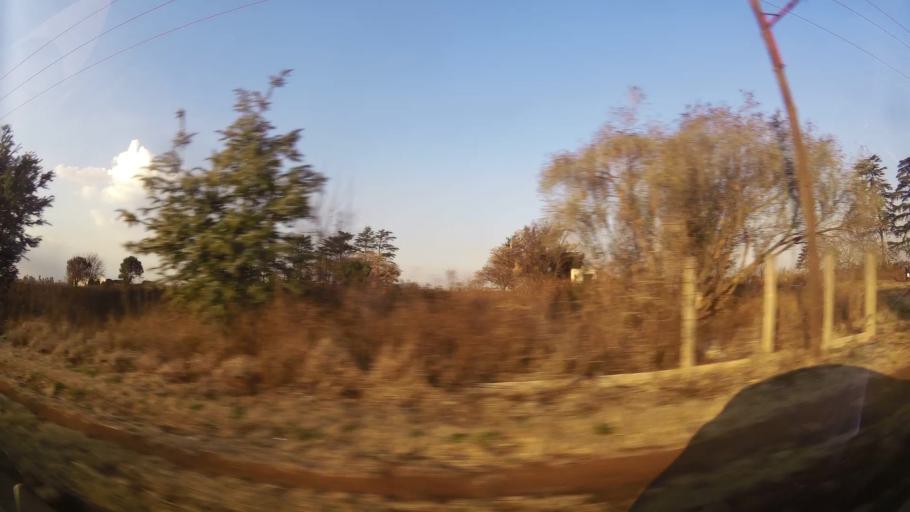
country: ZA
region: Gauteng
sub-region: Ekurhuleni Metropolitan Municipality
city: Germiston
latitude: -26.2971
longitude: 28.2312
